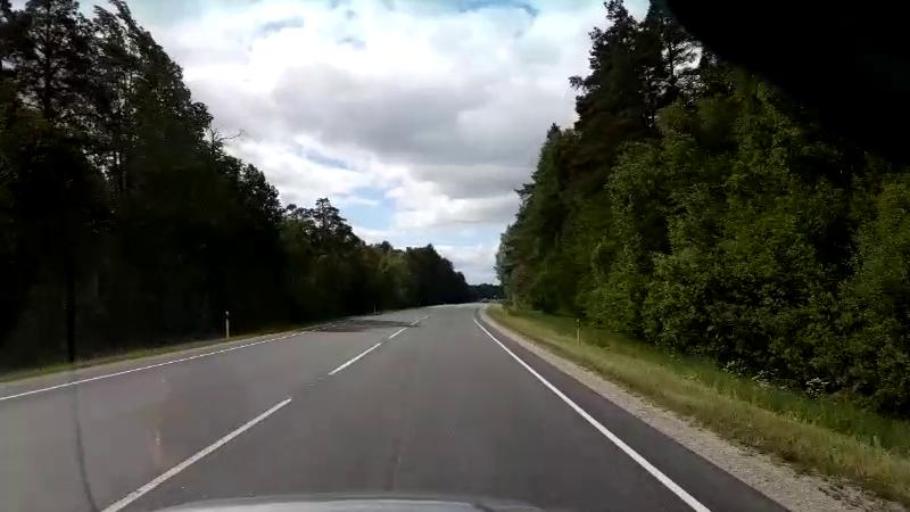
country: EE
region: Paernumaa
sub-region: Halinga vald
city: Parnu-Jaagupi
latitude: 58.6786
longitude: 24.4426
